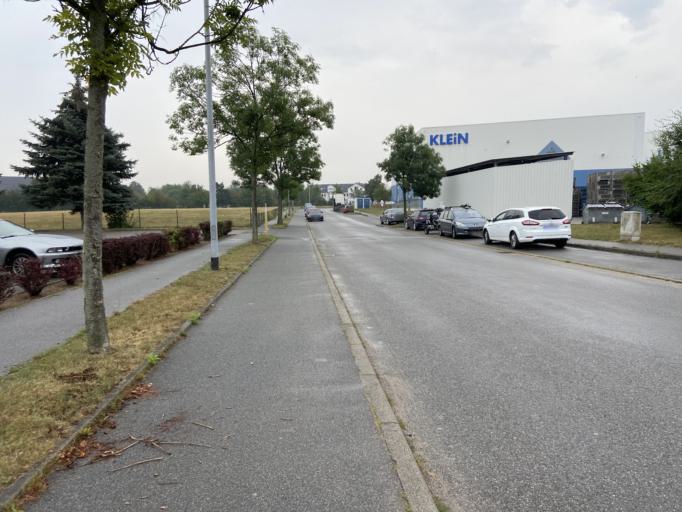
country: DE
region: Saxony
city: Ottendorf-Okrilla
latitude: 51.1821
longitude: 13.8413
